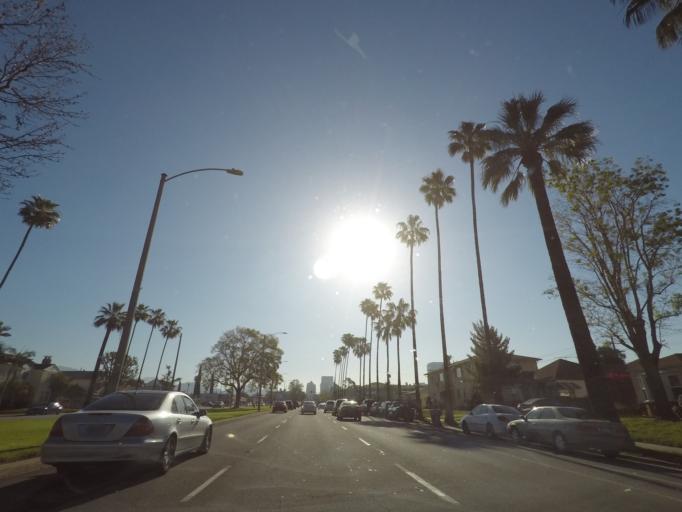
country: US
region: California
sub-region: Los Angeles County
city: North Glendale
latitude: 34.1597
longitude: -118.2689
